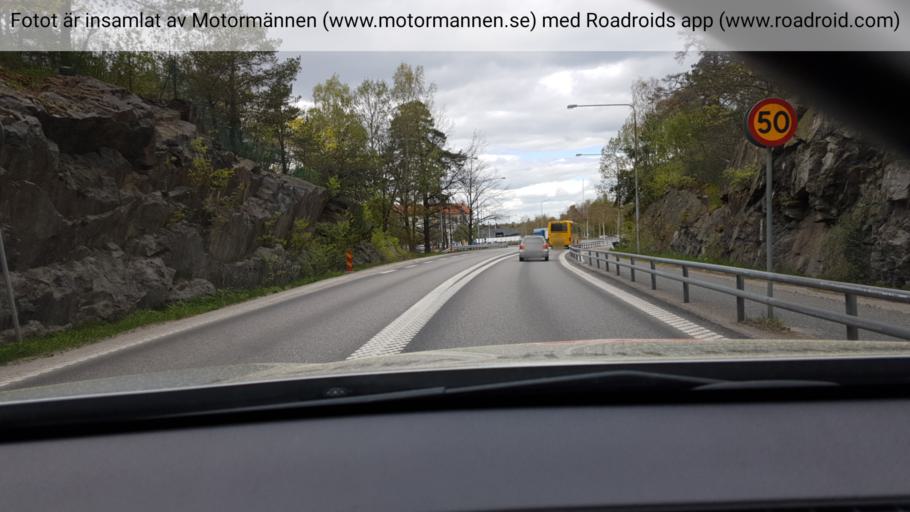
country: SE
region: Stockholm
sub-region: Tyreso Kommun
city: Bollmora
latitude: 59.2215
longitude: 18.2017
